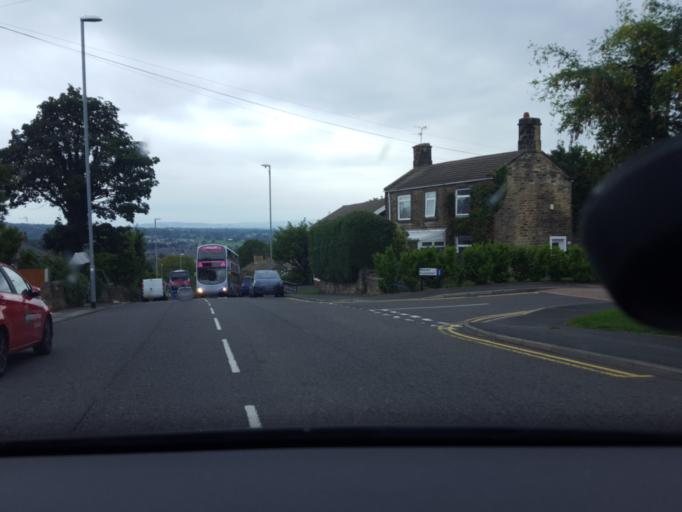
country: GB
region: England
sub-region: City and Borough of Leeds
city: Horsforth
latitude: 53.8155
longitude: -1.6374
